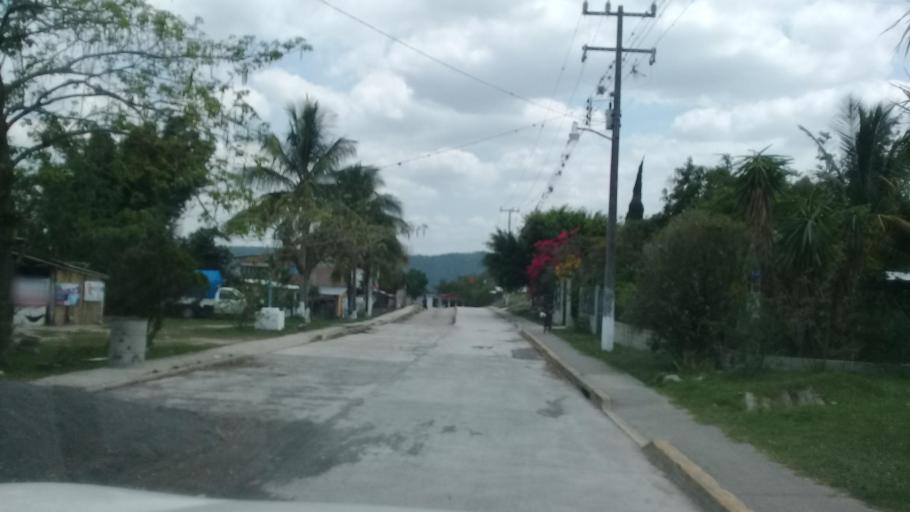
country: MX
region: Veracruz
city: Jalcomulco
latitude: 19.3920
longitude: -96.7895
